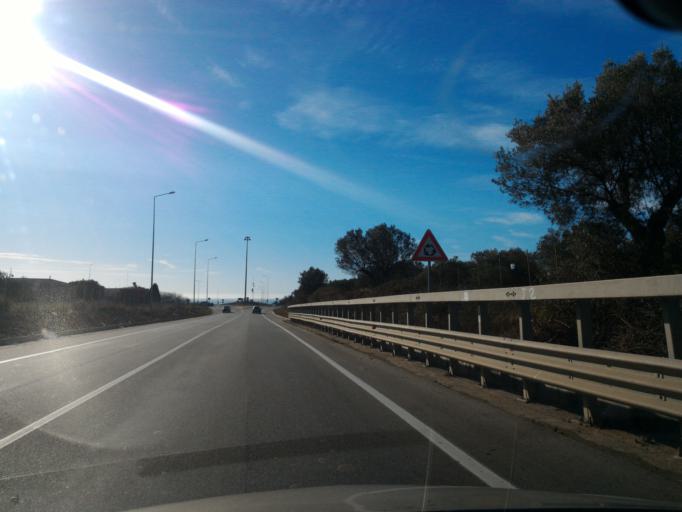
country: IT
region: Calabria
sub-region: Provincia di Crotone
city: Isola di Capo Rizzuto
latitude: 38.9529
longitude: 17.0825
